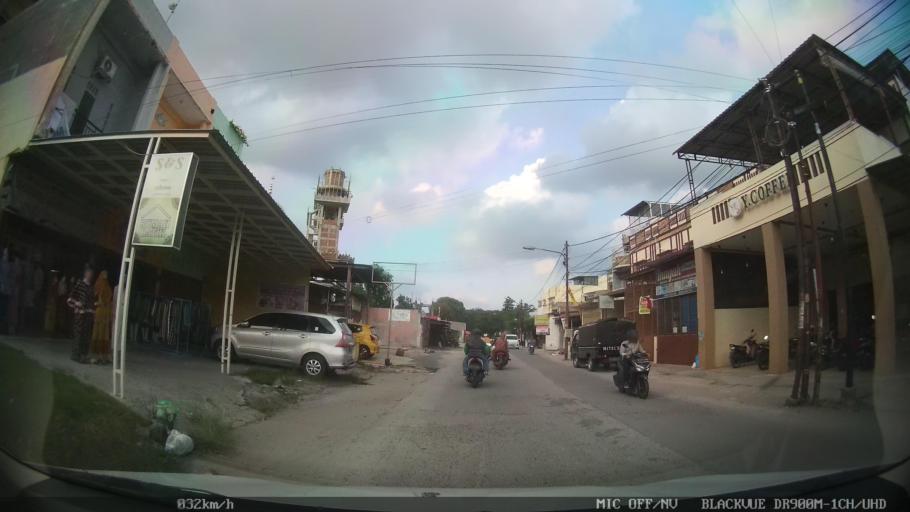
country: ID
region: North Sumatra
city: Medan
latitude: 3.5821
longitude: 98.7300
